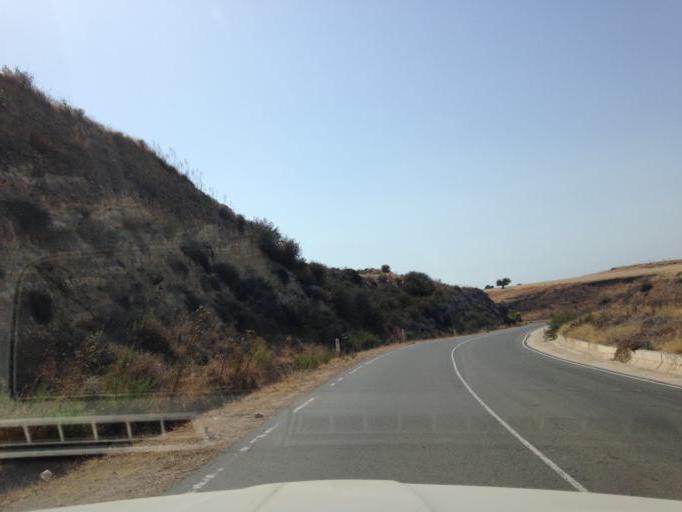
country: CY
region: Pafos
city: Mesogi
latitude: 34.7200
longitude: 32.5604
